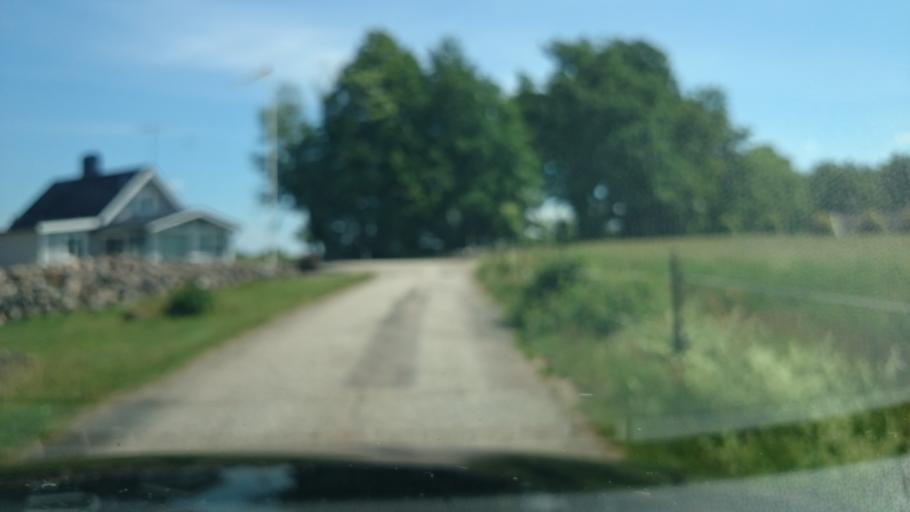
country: SE
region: Halland
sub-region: Hylte Kommun
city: Hyltebruk
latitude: 56.9649
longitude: 13.1947
